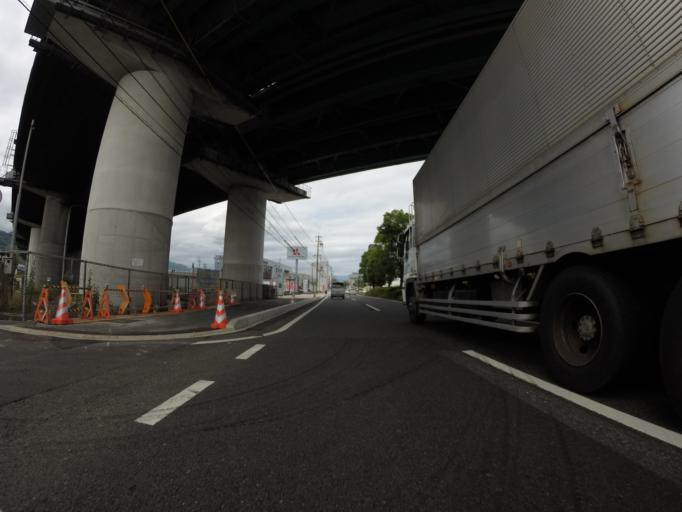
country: JP
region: Shizuoka
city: Shizuoka-shi
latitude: 35.0003
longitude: 138.4330
